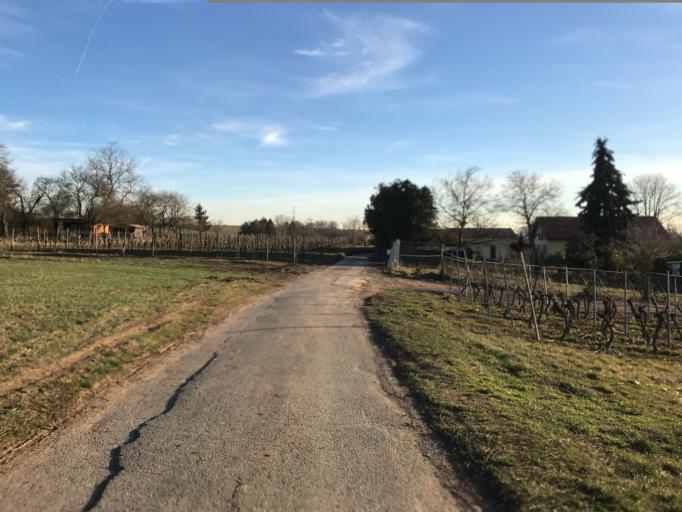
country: DE
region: Rheinland-Pfalz
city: Mainz
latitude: 49.9590
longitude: 8.2842
